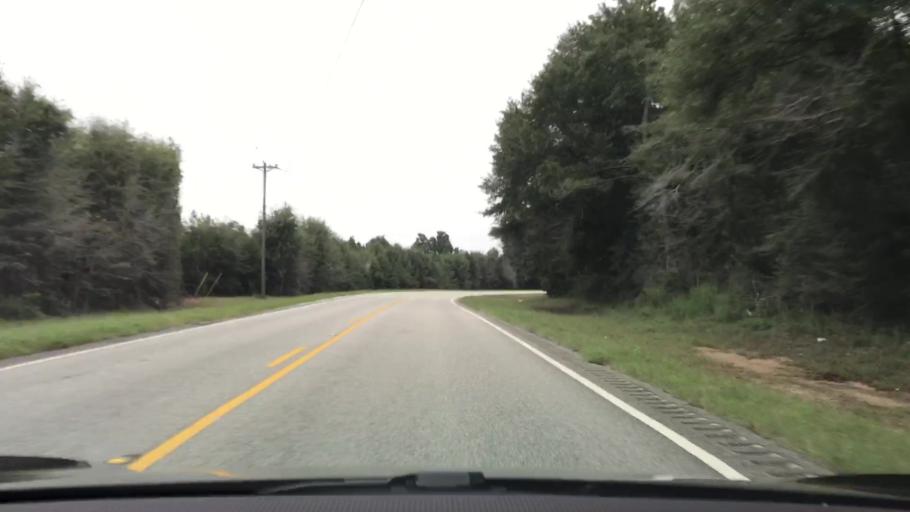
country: US
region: Alabama
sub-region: Coffee County
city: Elba
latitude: 31.3774
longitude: -86.0915
